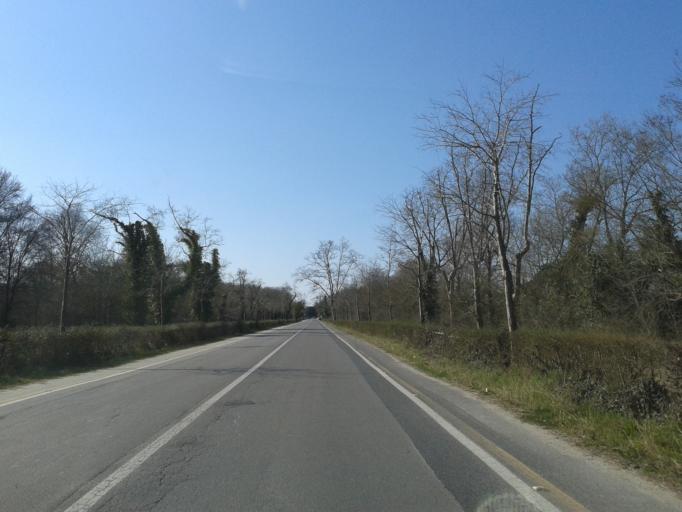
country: IT
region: Tuscany
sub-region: Province of Pisa
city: Madonna dell'Acqua
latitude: 43.7220
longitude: 10.3500
